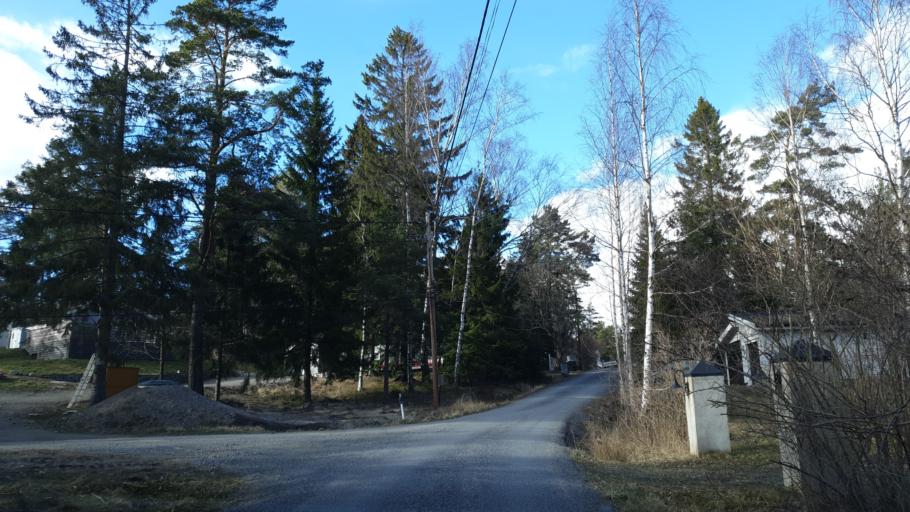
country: SE
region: Stockholm
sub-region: Varmdo Kommun
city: Holo
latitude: 59.2778
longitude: 18.6356
